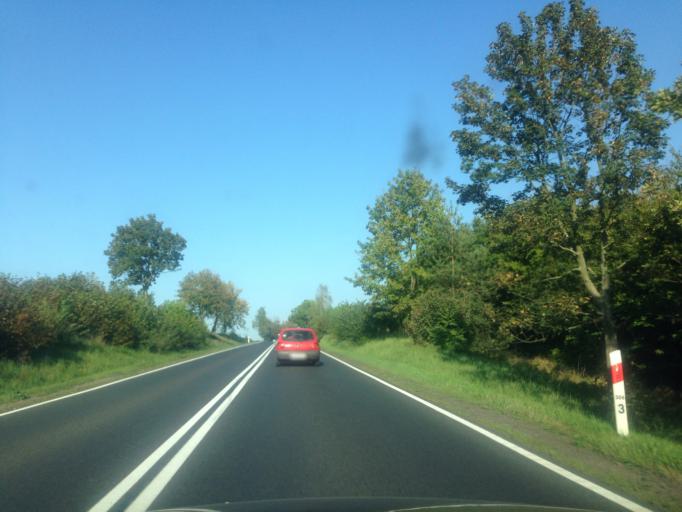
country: PL
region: Kujawsko-Pomorskie
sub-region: Powiat brodnicki
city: Brodnica
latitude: 53.2877
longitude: 19.4899
